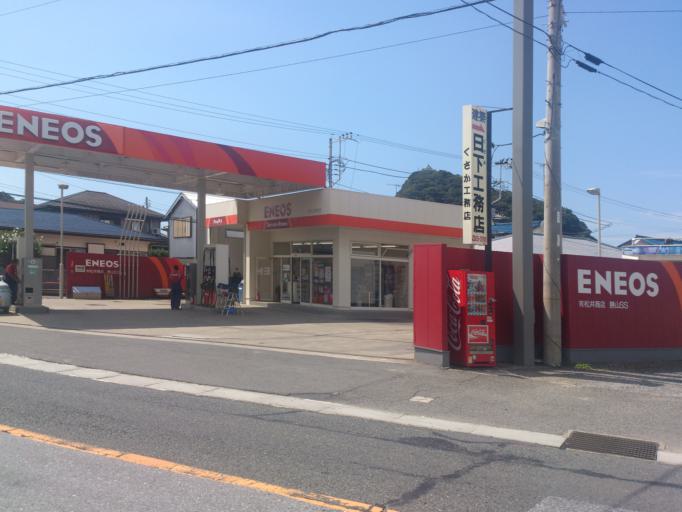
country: JP
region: Chiba
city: Tateyama
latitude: 35.1149
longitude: 139.8326
